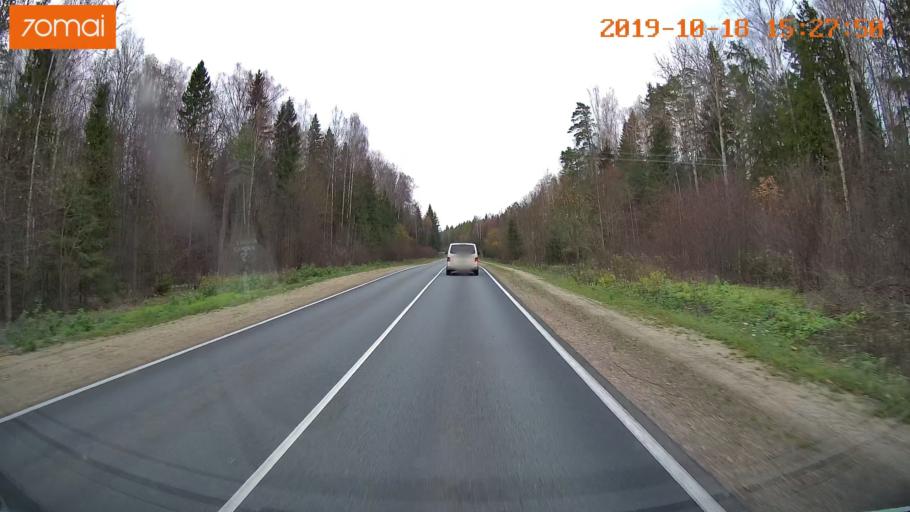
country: RU
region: Vladimir
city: Anopino
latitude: 55.7585
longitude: 40.6725
